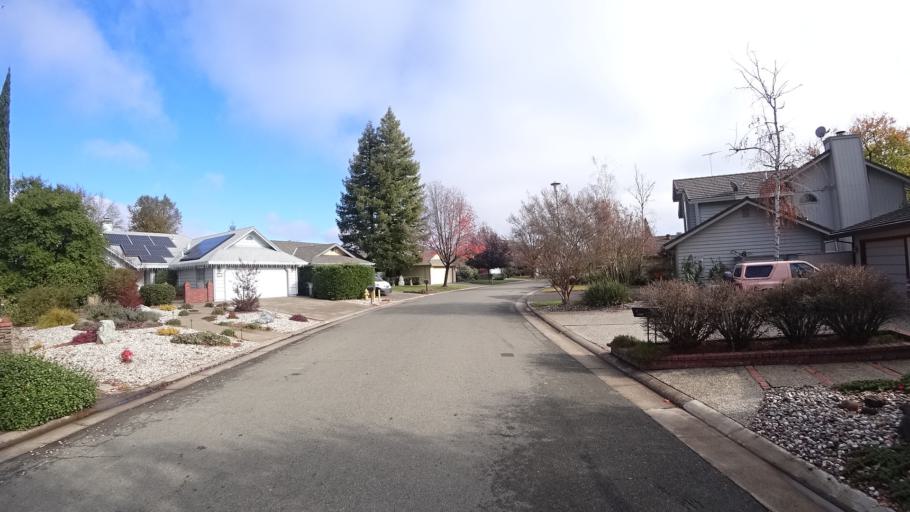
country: US
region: California
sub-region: Sacramento County
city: Antelope
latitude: 38.6849
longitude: -121.3223
